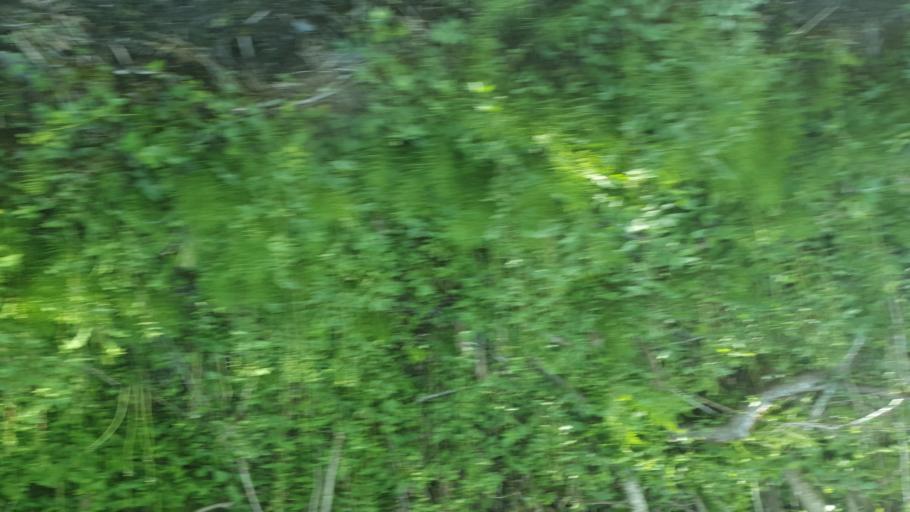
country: NO
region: Sor-Trondelag
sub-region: Rissa
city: Rissa
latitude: 63.4966
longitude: 10.0856
